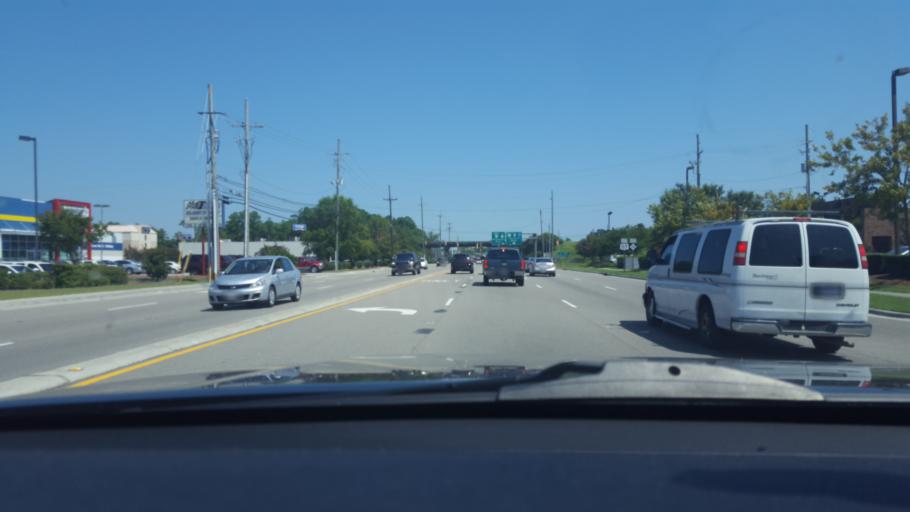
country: US
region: North Carolina
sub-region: New Hanover County
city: Kings Grant
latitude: 34.2455
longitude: -77.8741
